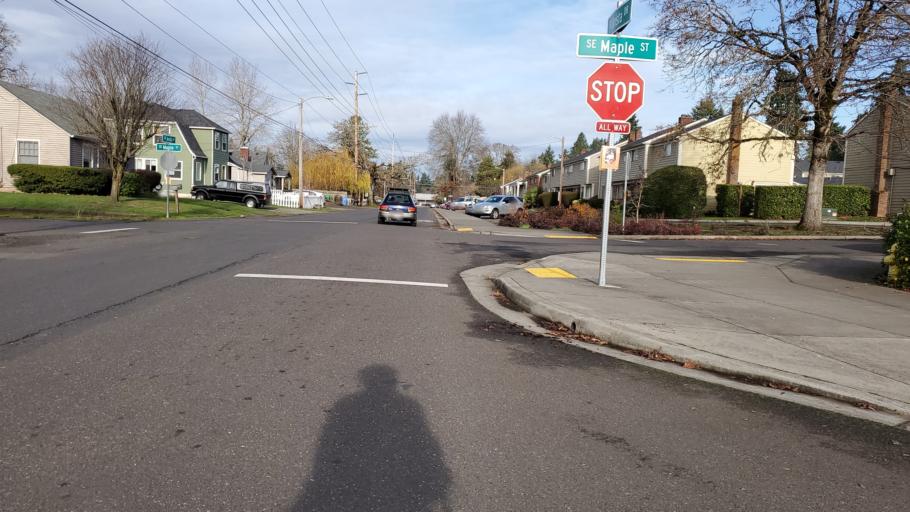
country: US
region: Oregon
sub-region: Clackamas County
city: Oak Grove
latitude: 45.4181
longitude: -122.6416
